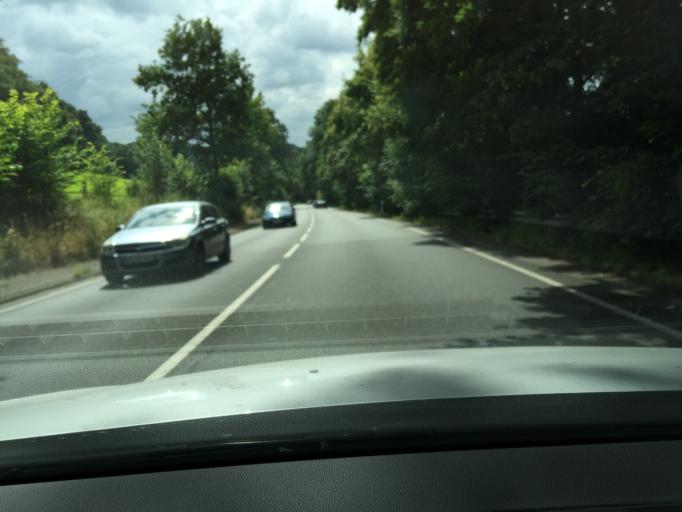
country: DE
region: North Rhine-Westphalia
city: Hattingen
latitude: 51.3773
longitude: 7.2096
